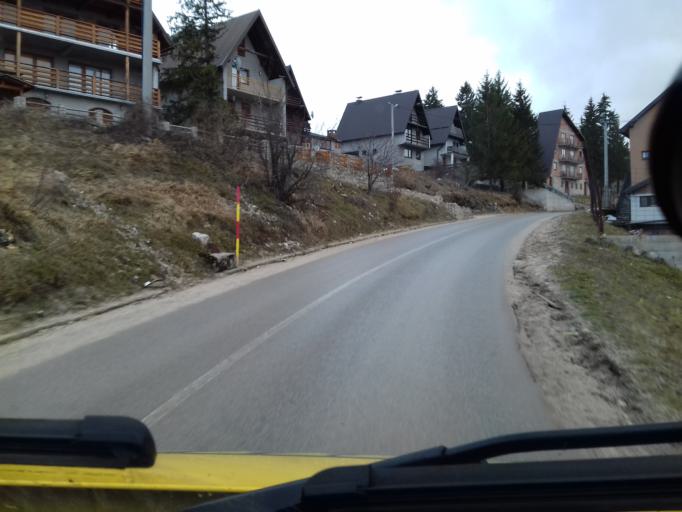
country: BA
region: Federation of Bosnia and Herzegovina
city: Turbe
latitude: 44.3109
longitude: 17.5714
